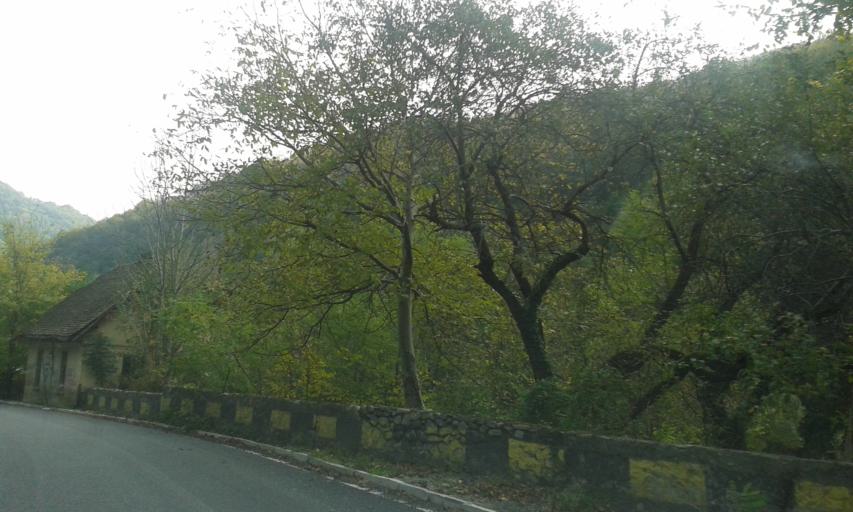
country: RO
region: Gorj
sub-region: Comuna Bumbesti-Jiu
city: Bumbesti-Jiu
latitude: 45.2706
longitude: 23.3764
